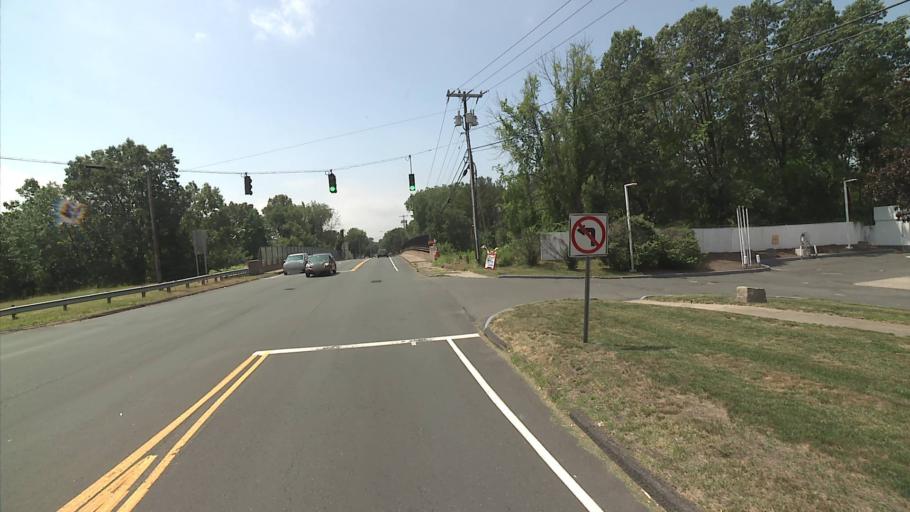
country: US
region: Connecticut
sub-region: Hartford County
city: Glastonbury Center
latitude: 41.7139
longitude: -72.5910
